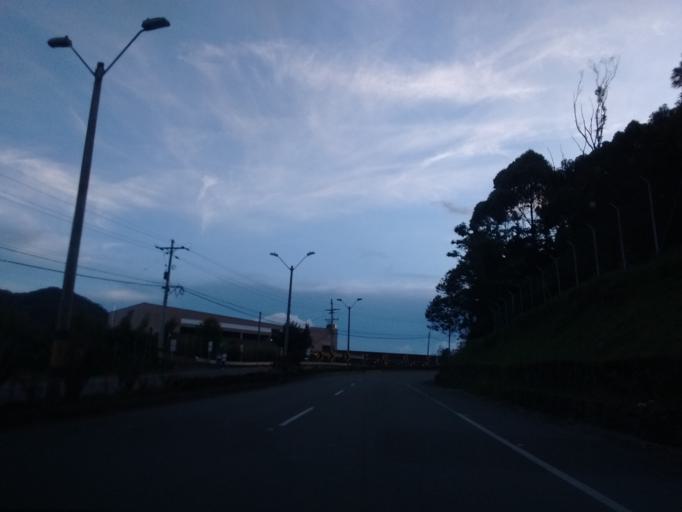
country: CO
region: Antioquia
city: Envigado
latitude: 6.1533
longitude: -75.5391
